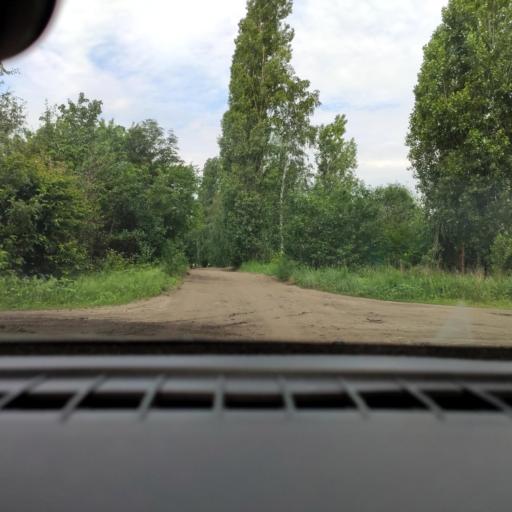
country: RU
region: Voronezj
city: Maslovka
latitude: 51.5018
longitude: 39.1950
